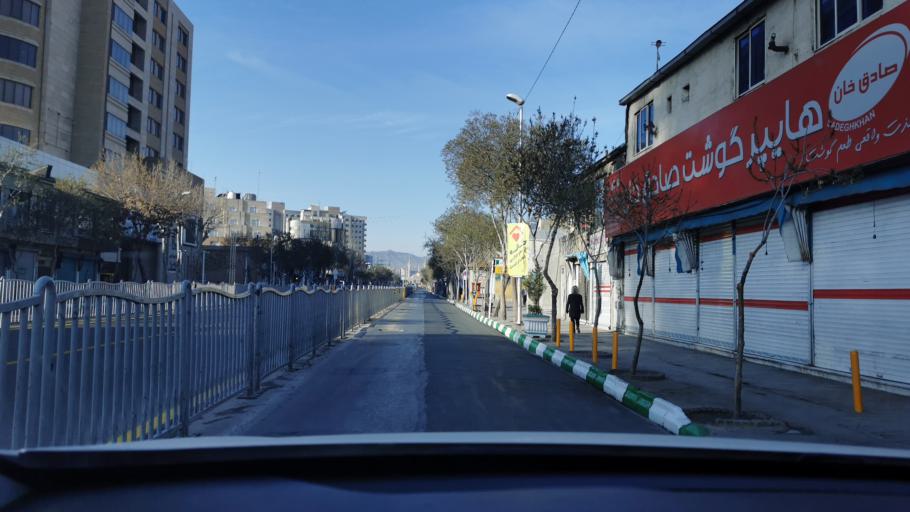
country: IR
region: Razavi Khorasan
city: Mashhad
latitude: 36.2951
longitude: 59.6269
